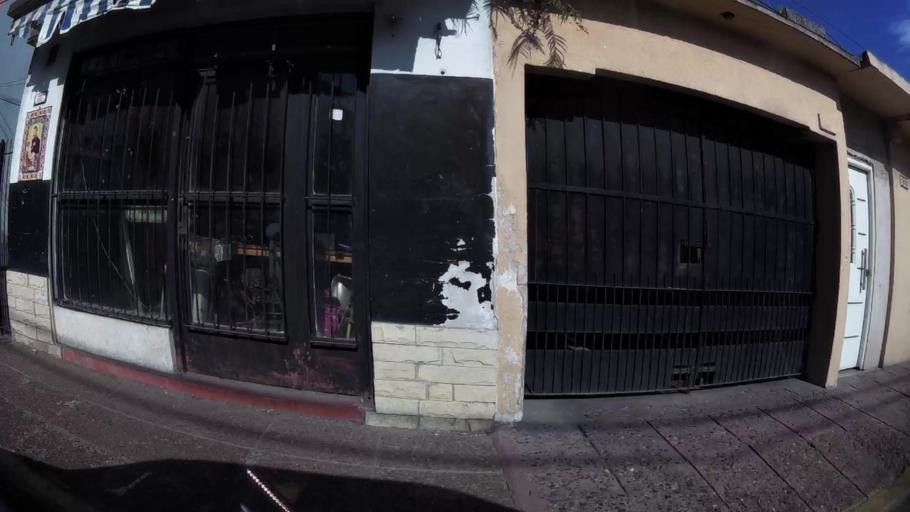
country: AR
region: Buenos Aires
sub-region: Partido de Merlo
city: Merlo
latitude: -34.6650
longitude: -58.7144
